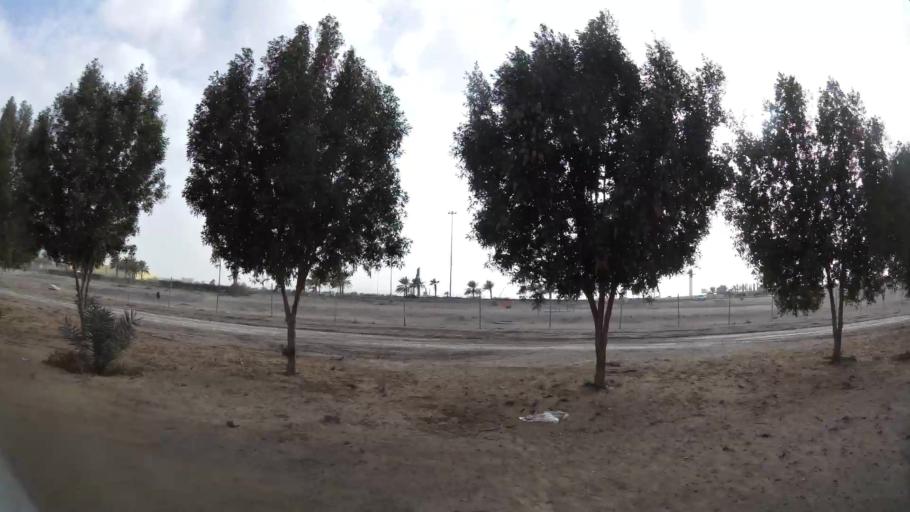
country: AE
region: Abu Dhabi
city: Abu Dhabi
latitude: 24.5004
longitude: 54.5957
